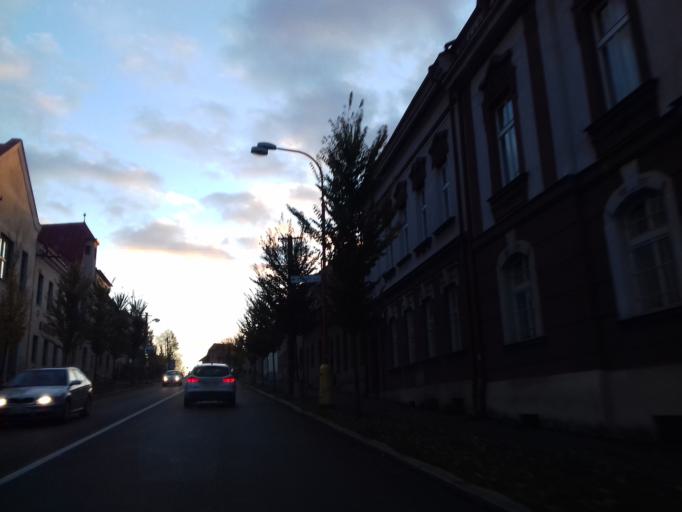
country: CZ
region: Pardubicky
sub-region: Okres Chrudim
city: Hlinsko
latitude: 49.7589
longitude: 15.9045
